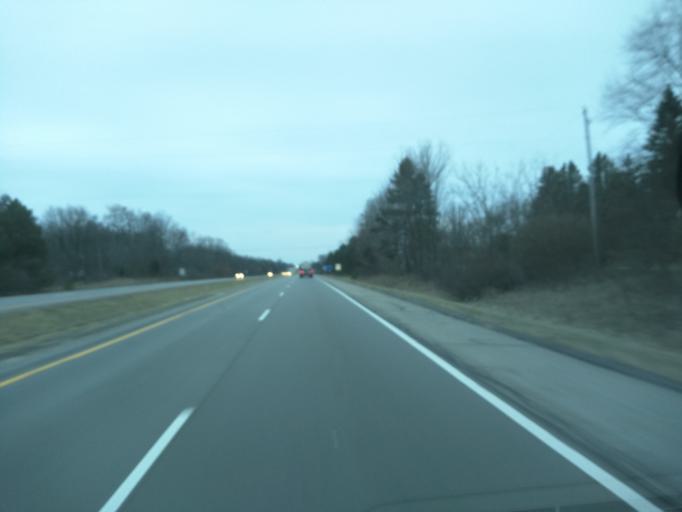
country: US
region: Michigan
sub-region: Ingham County
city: Leslie
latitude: 42.3944
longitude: -84.4293
